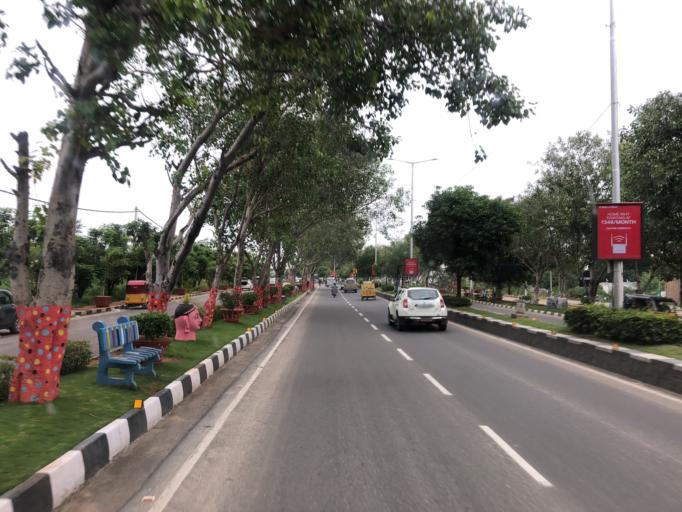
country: IN
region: Telangana
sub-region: Rangareddi
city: Kukatpalli
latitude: 17.4614
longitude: 78.3766
